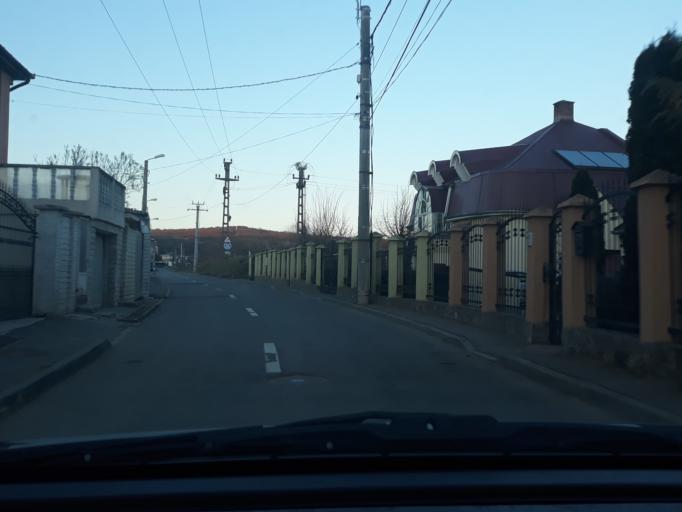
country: RO
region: Bihor
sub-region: Comuna Biharea
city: Oradea
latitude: 47.0801
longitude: 21.9450
